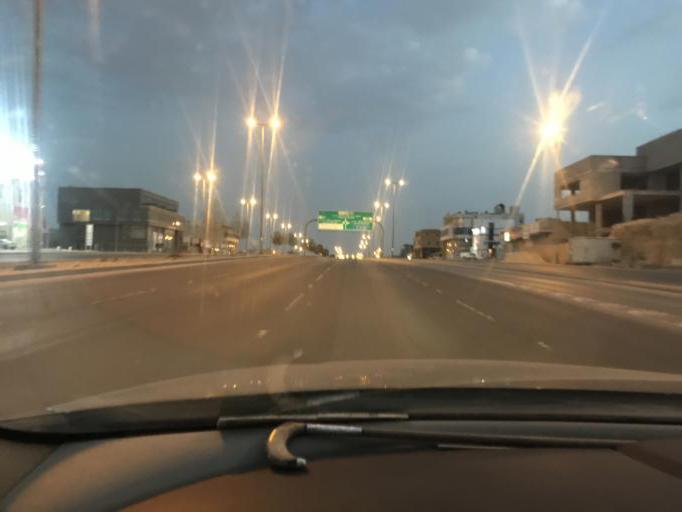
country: SA
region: Ar Riyad
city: Riyadh
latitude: 24.8401
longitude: 46.6765
